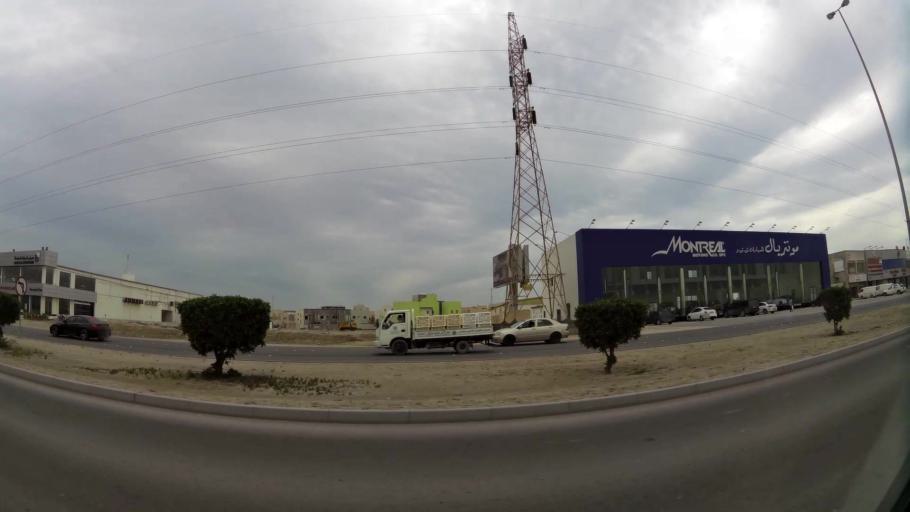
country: BH
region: Northern
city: Sitrah
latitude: 26.1542
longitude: 50.6127
